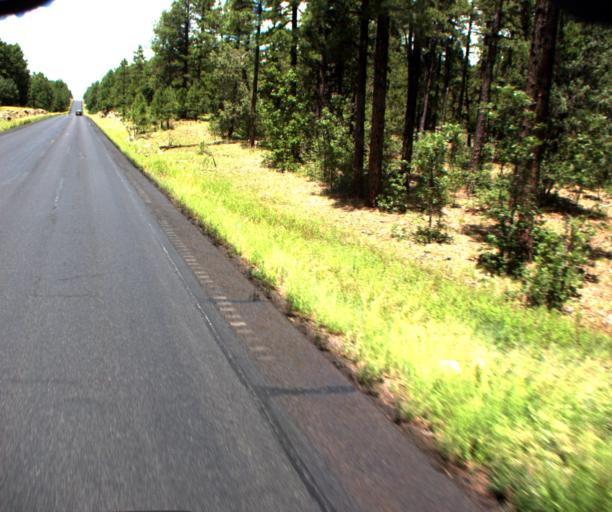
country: US
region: Arizona
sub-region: Gila County
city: Pine
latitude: 34.4793
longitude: -111.4524
